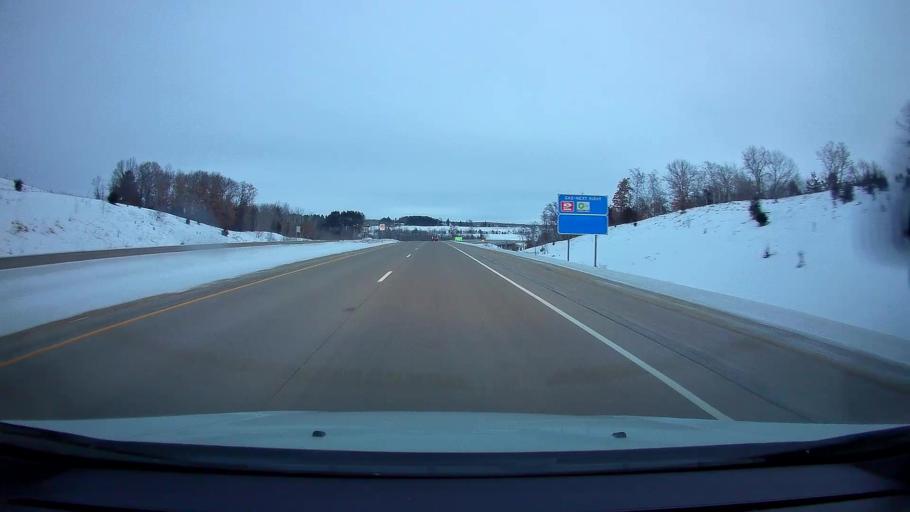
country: US
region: Wisconsin
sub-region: Saint Croix County
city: Somerset
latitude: 45.1136
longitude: -92.6672
